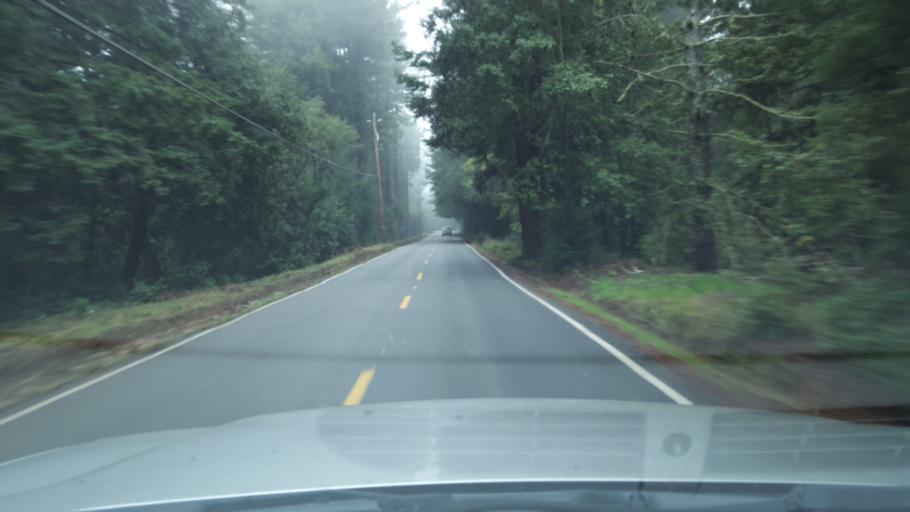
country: US
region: California
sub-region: Santa Cruz County
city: Interlaken
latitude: 37.0263
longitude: -121.7366
